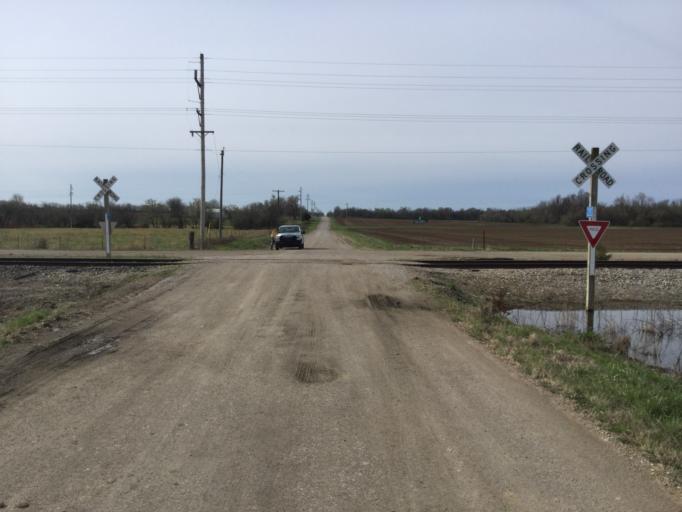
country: US
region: Kansas
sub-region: Cherokee County
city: Columbus
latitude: 37.1789
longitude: -94.9043
